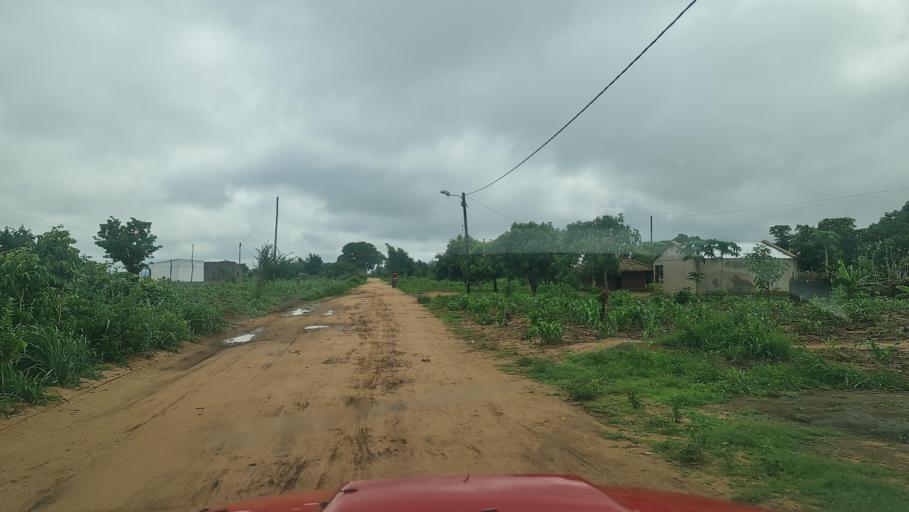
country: MW
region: Southern Region
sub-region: Nsanje District
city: Nsanje
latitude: -17.1901
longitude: 35.7102
